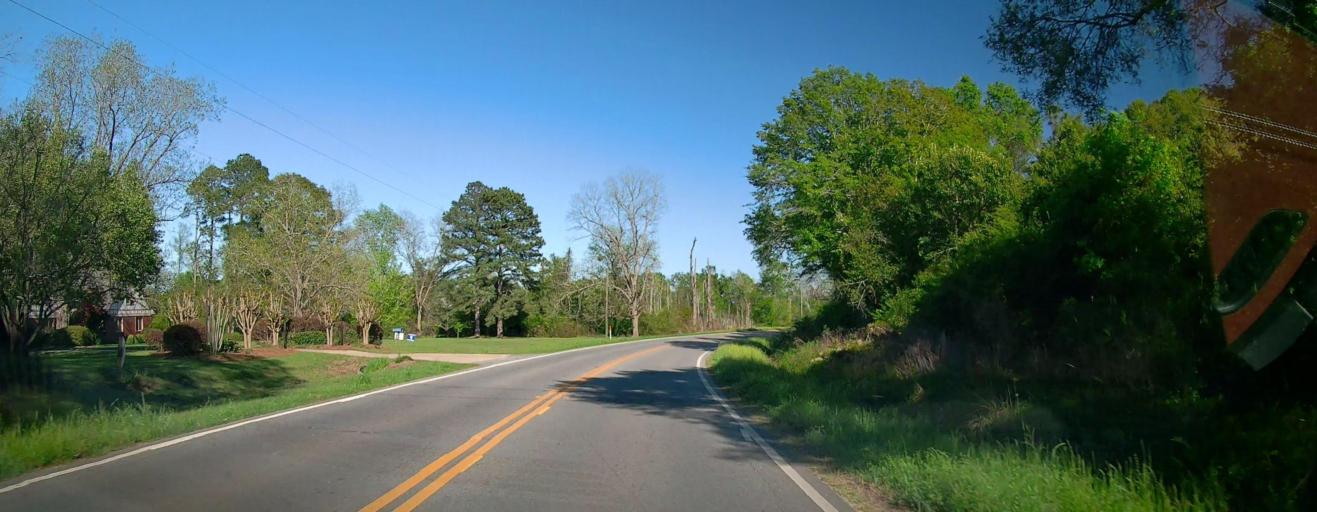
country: US
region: Georgia
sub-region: Wilcox County
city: Rochelle
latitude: 31.9462
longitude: -83.4468
